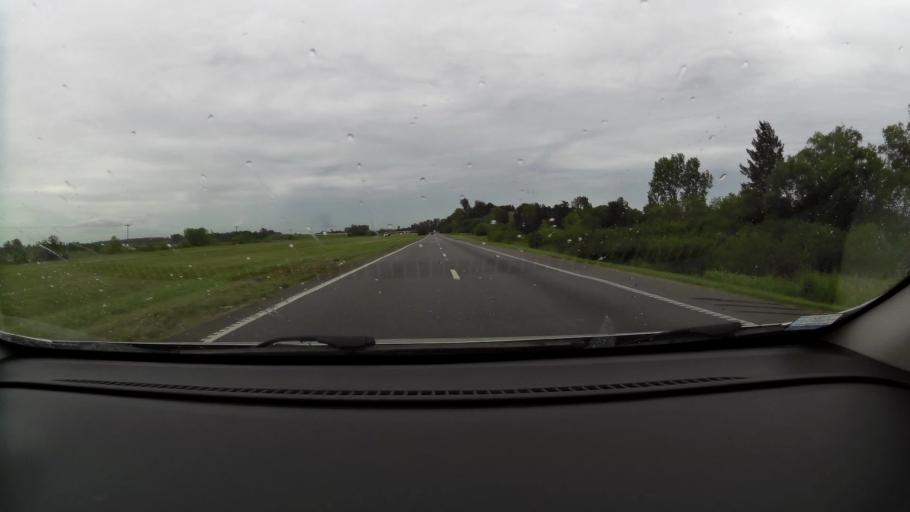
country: AR
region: Buenos Aires
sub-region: Partido de Baradero
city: Baradero
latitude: -33.9514
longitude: -59.3998
